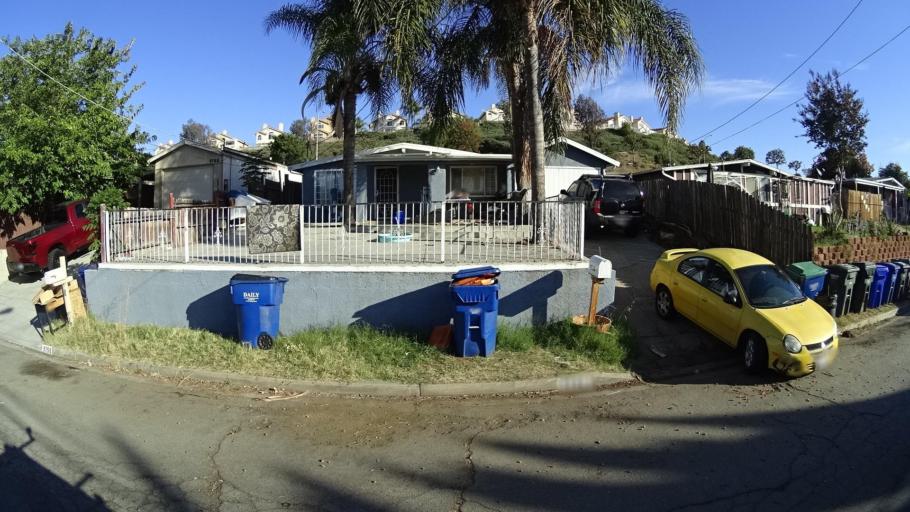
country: US
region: California
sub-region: San Diego County
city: La Presa
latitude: 32.7108
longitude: -116.9868
